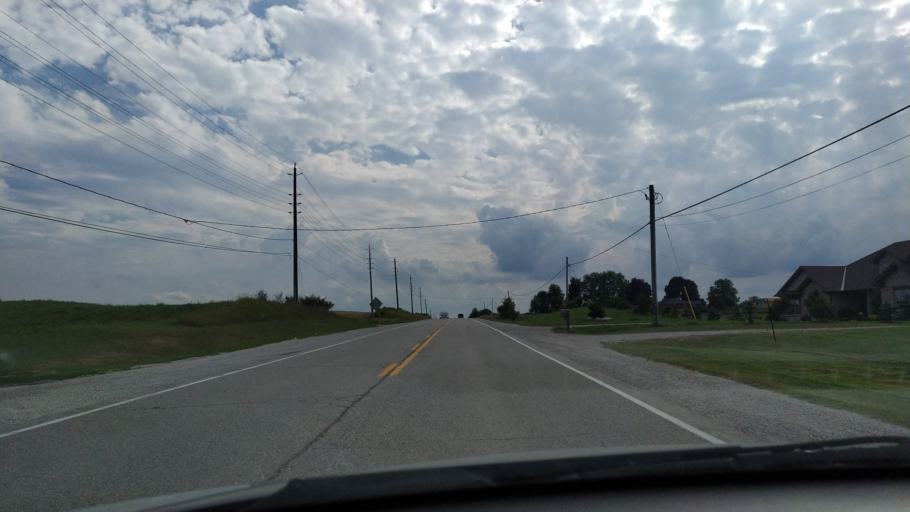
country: CA
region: Ontario
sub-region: Wellington County
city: Guelph
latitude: 43.4663
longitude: -80.1640
